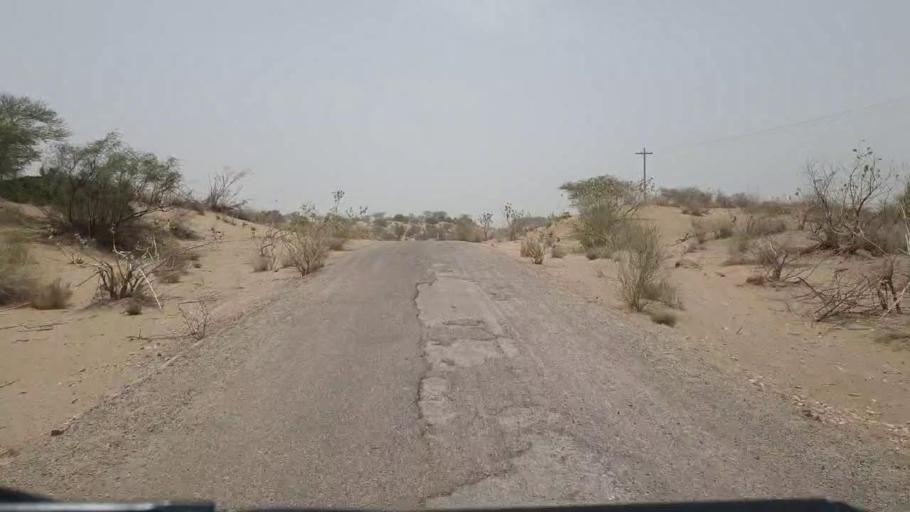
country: PK
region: Sindh
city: Naukot
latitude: 24.7434
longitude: 69.5485
